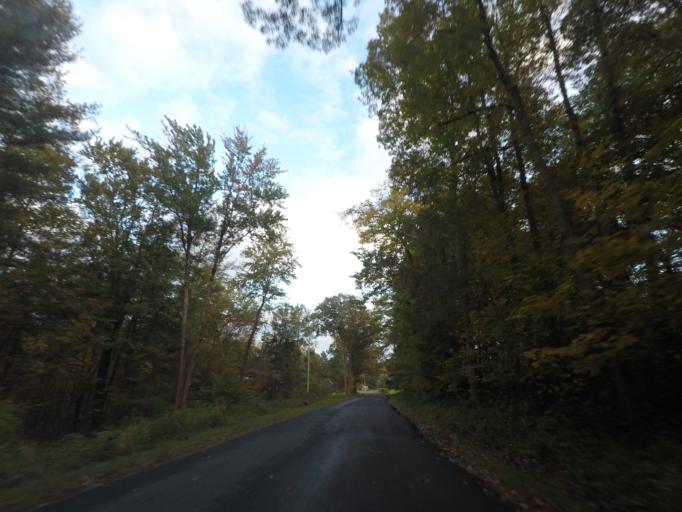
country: US
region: New York
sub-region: Rensselaer County
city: Nassau
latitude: 42.5377
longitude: -73.5765
